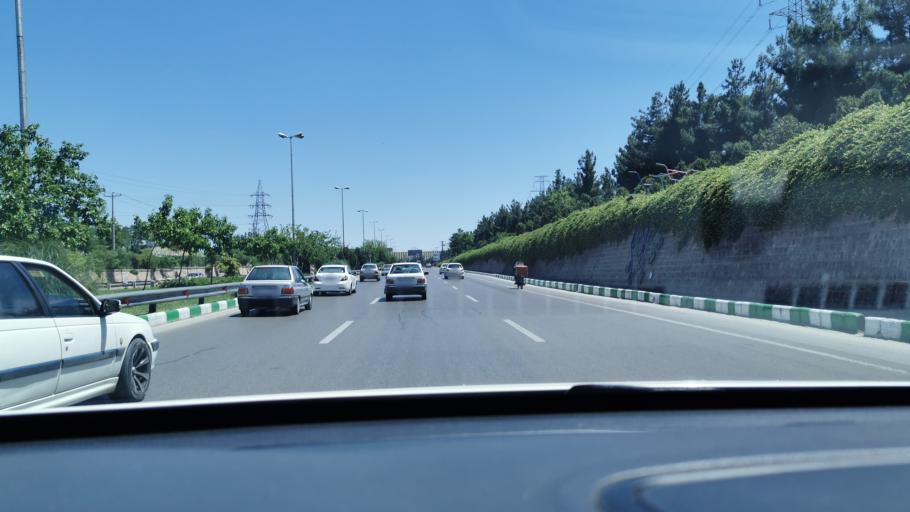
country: IR
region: Razavi Khorasan
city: Mashhad
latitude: 36.2618
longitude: 59.5840
